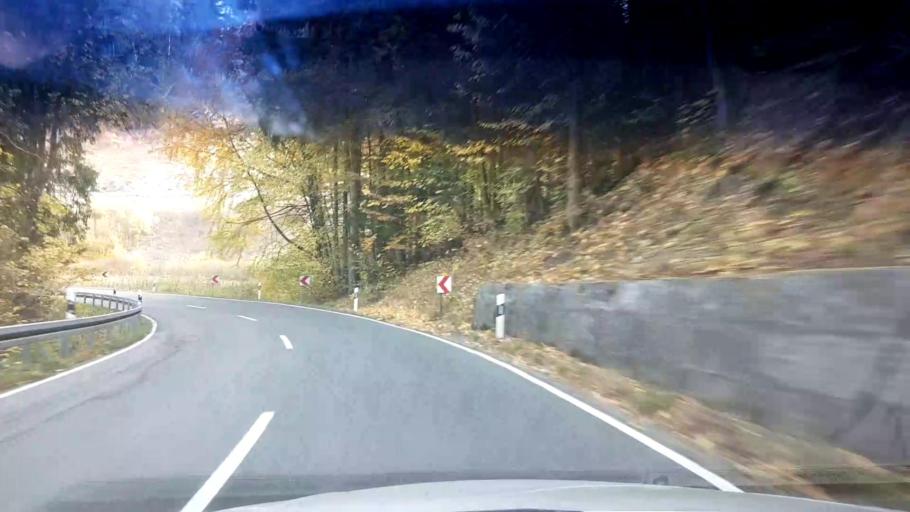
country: DE
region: Bavaria
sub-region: Upper Franconia
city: Weismain
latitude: 50.0458
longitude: 11.2290
